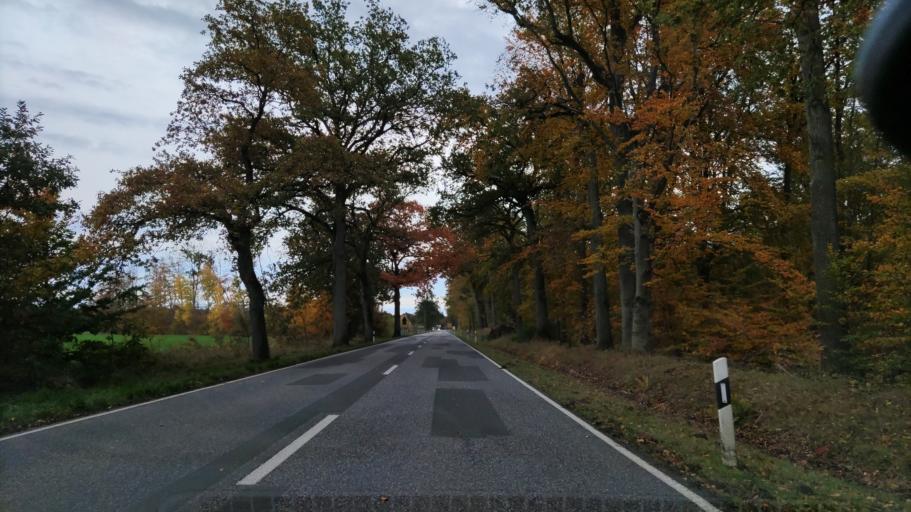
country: DE
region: Mecklenburg-Vorpommern
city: Lubtheen
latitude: 53.3610
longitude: 11.1350
